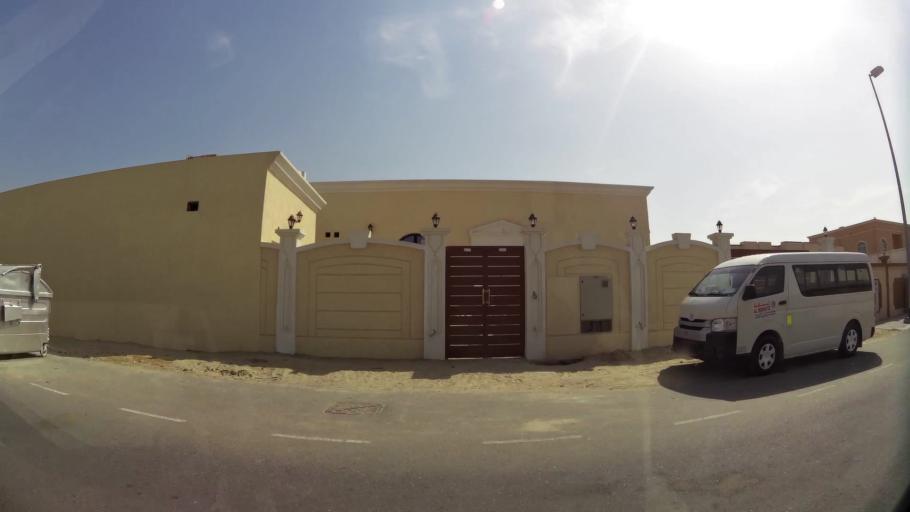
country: AE
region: Ash Shariqah
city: Sharjah
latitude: 25.2784
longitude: 55.3994
